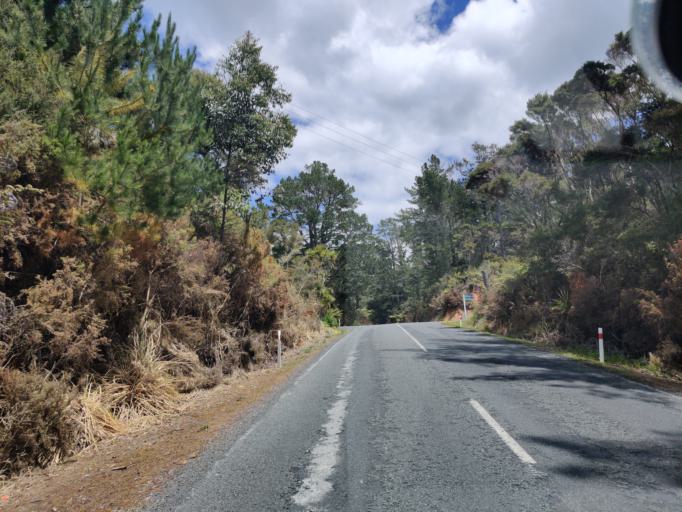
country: NZ
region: Northland
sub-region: Far North District
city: Paihia
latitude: -35.2931
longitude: 174.1387
